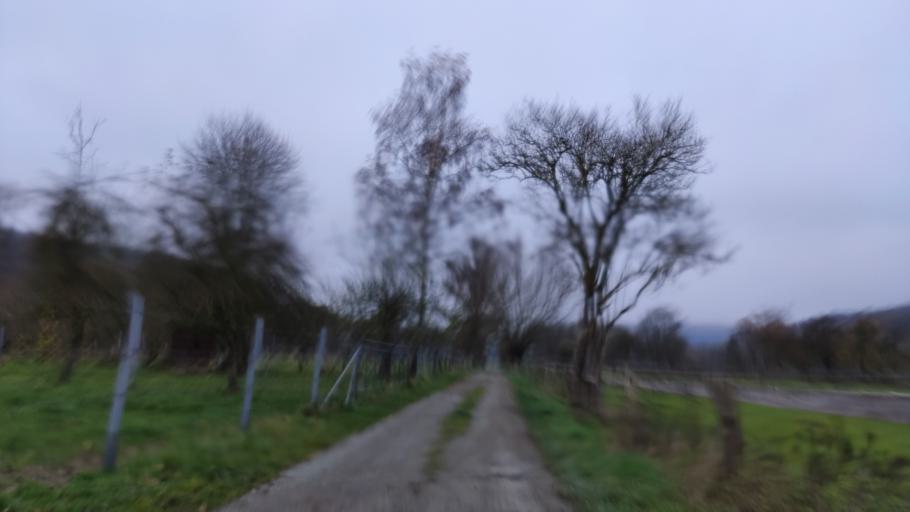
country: DE
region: North Rhine-Westphalia
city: Beverungen
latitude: 51.7078
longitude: 9.2895
